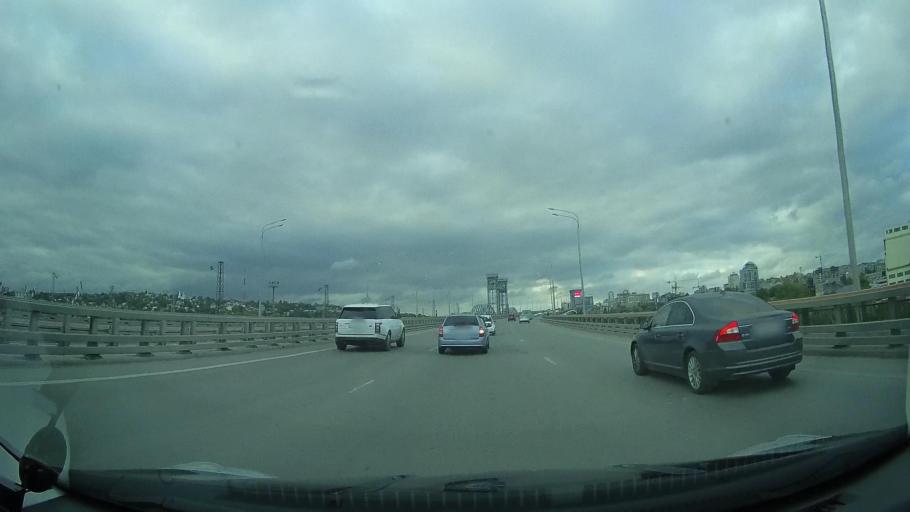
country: RU
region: Rostov
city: Rostov-na-Donu
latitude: 47.2059
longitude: 39.7062
